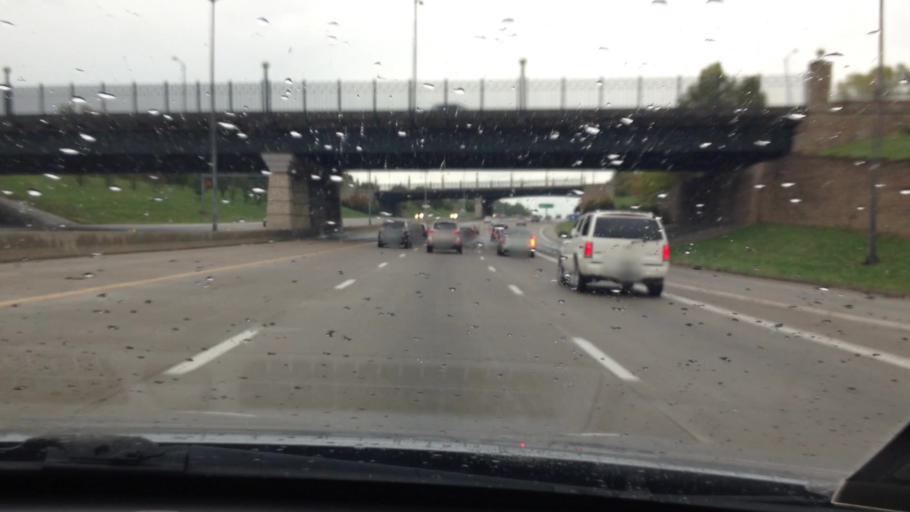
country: US
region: Missouri
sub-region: Jackson County
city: Kansas City
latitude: 39.0709
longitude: -94.5606
